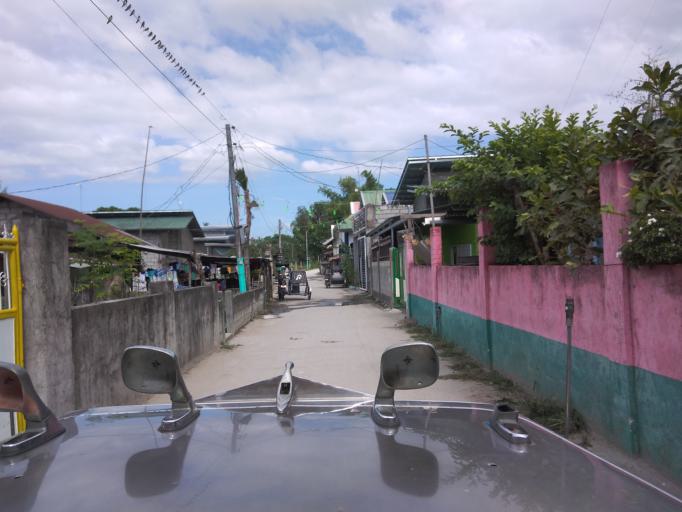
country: PH
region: Central Luzon
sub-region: Province of Pampanga
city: San Patricio
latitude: 15.1112
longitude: 120.7190
